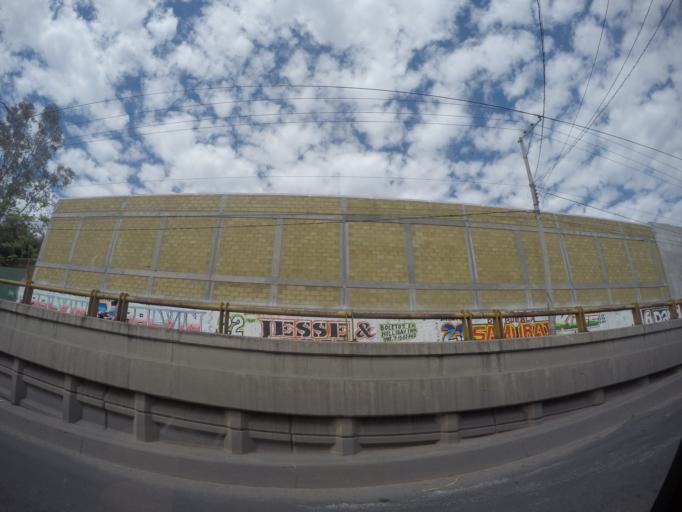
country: MX
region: Guanajuato
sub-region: Leon
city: San Jose de Duran (Los Troncoso)
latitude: 21.0935
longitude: -101.6794
